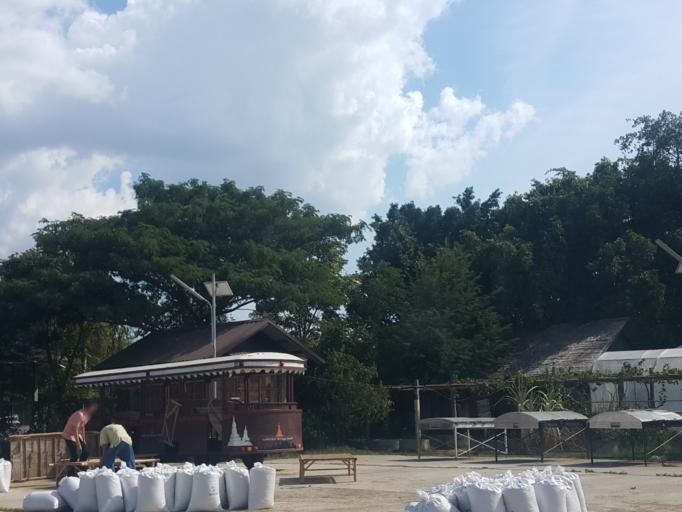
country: TH
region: Sukhothai
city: Si Samrong
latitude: 17.2287
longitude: 99.8255
